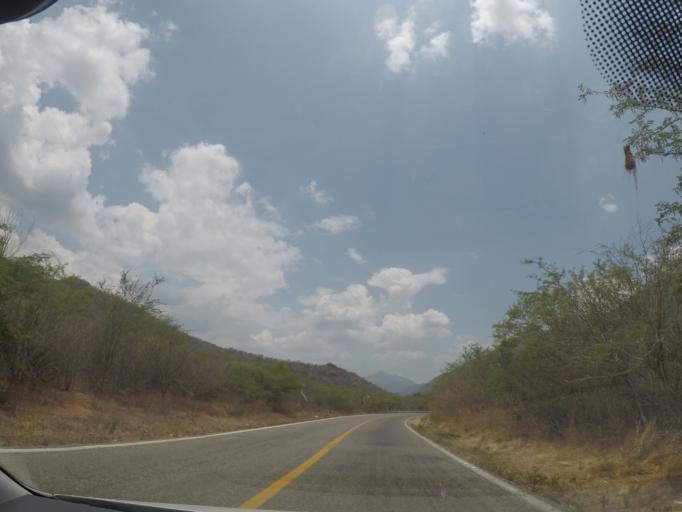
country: MX
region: Oaxaca
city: Santa Maria Mixtequilla
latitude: 16.3502
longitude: -95.3330
